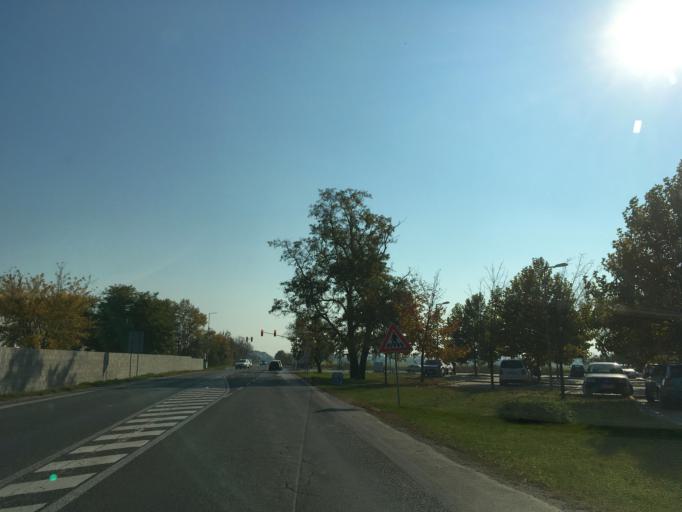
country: SK
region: Bratislavsky
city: Dunajska Luzna
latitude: 48.0770
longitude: 17.2699
